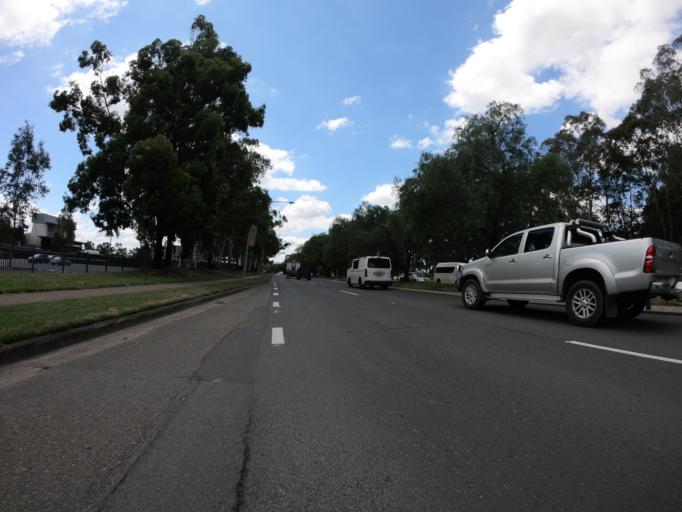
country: AU
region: New South Wales
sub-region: Penrith Municipality
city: Penrith
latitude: -33.7587
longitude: 150.6851
